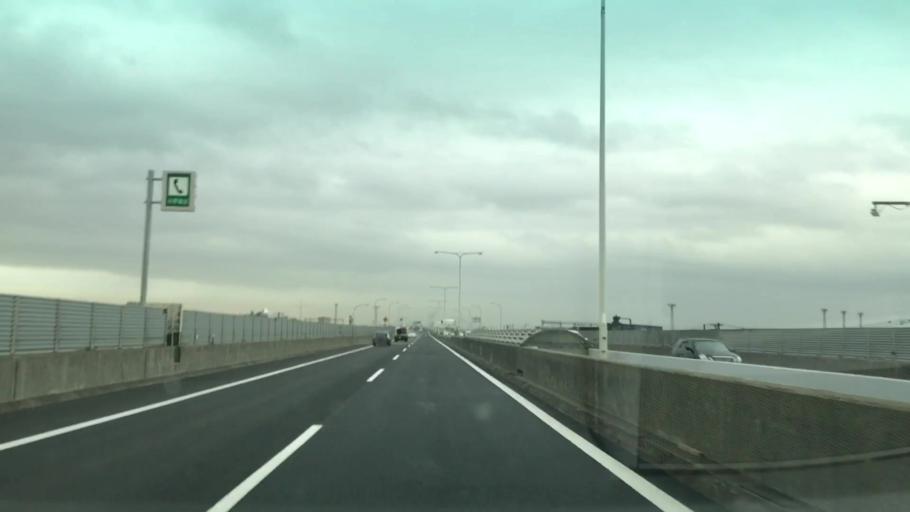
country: JP
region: Hokkaido
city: Sapporo
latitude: 43.0401
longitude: 141.4388
